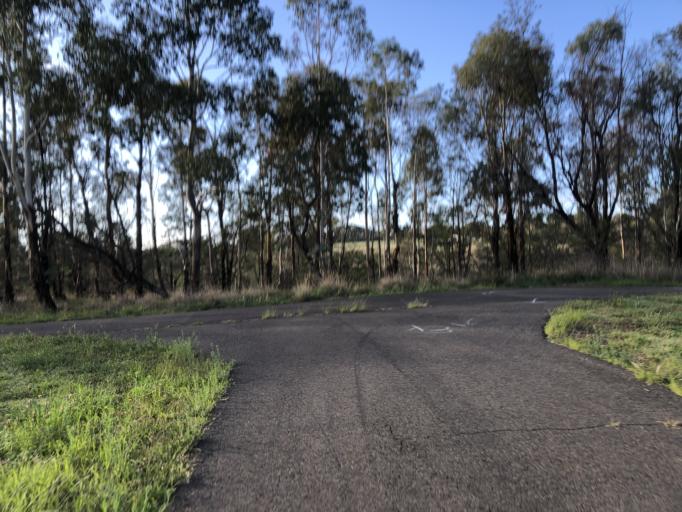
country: AU
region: New South Wales
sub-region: Orange Municipality
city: Orange
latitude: -33.3290
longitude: 149.0848
